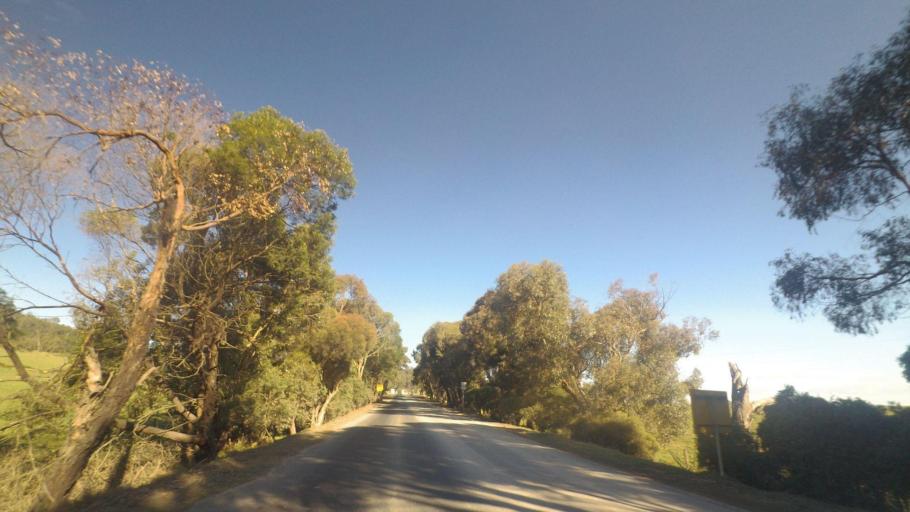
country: AU
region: Victoria
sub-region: Knox
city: Rowville
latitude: -37.9304
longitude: 145.2623
